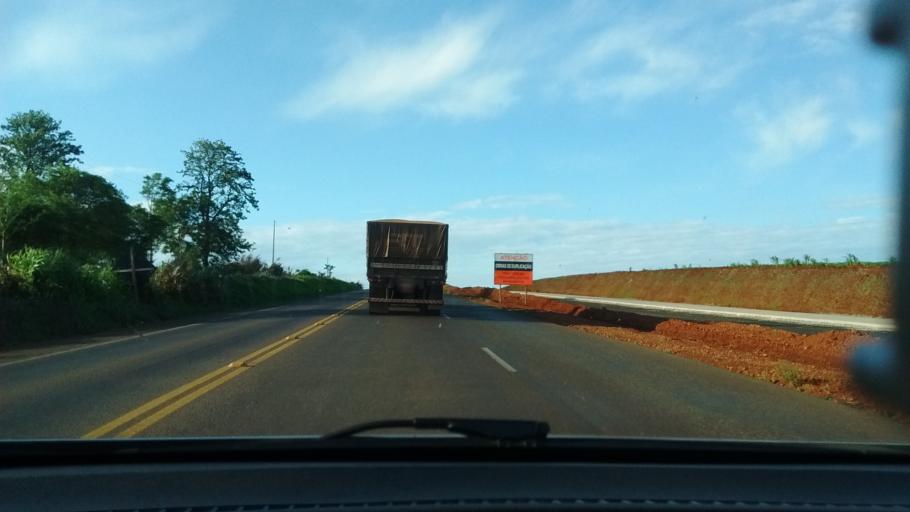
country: BR
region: Parana
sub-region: Cascavel
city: Cascavel
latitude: -25.1484
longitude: -53.5923
